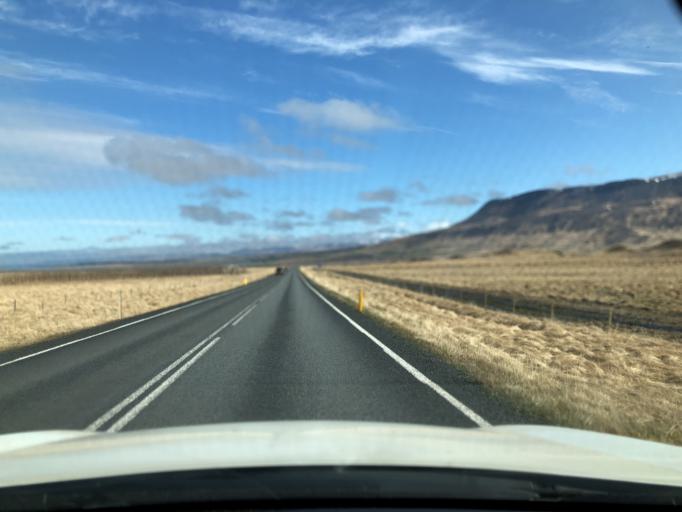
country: IS
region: Northwest
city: Saudarkrokur
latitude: 65.4965
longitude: -20.4058
